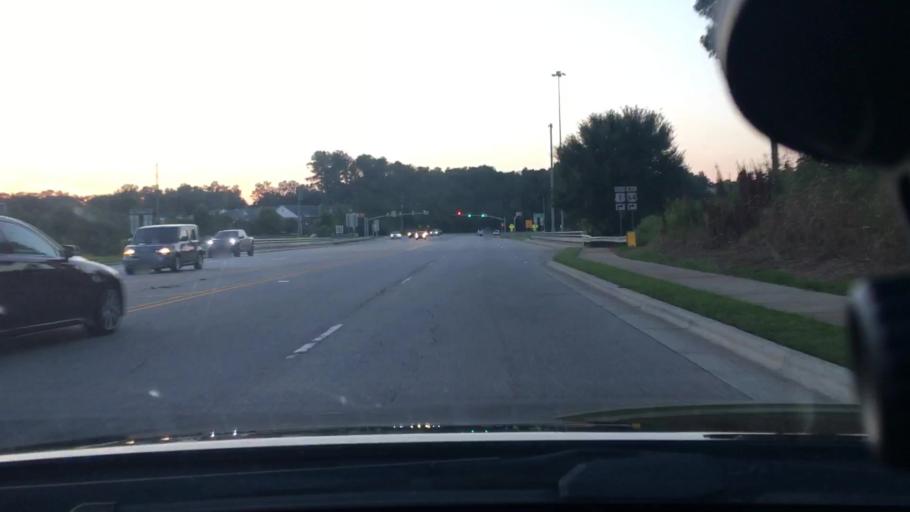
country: US
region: North Carolina
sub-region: Wake County
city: Cary
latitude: 35.7481
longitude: -78.7711
